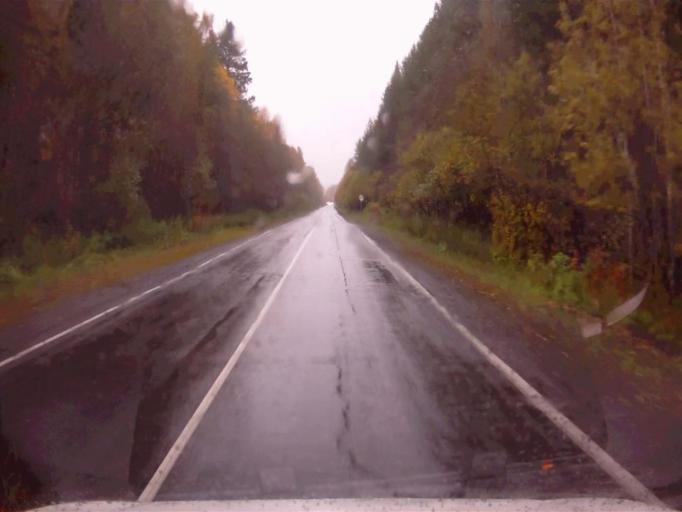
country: RU
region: Chelyabinsk
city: Verkhniy Ufaley
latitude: 55.9371
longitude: 60.4133
